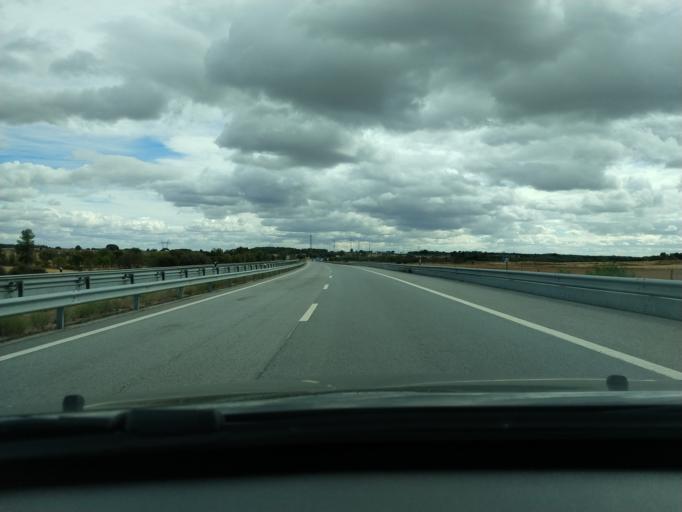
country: PT
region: Guarda
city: Alcains
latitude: 40.0120
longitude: -7.4663
